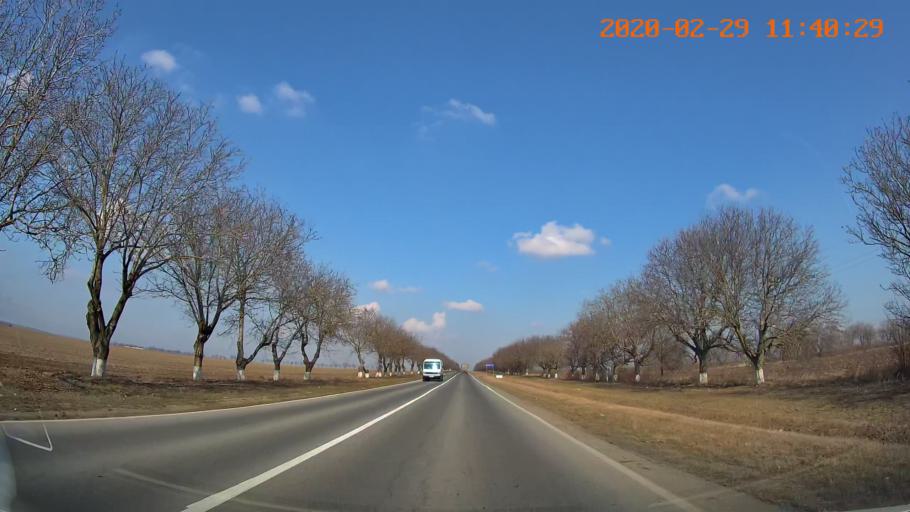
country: MD
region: Rezina
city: Saharna
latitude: 47.6572
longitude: 29.0200
